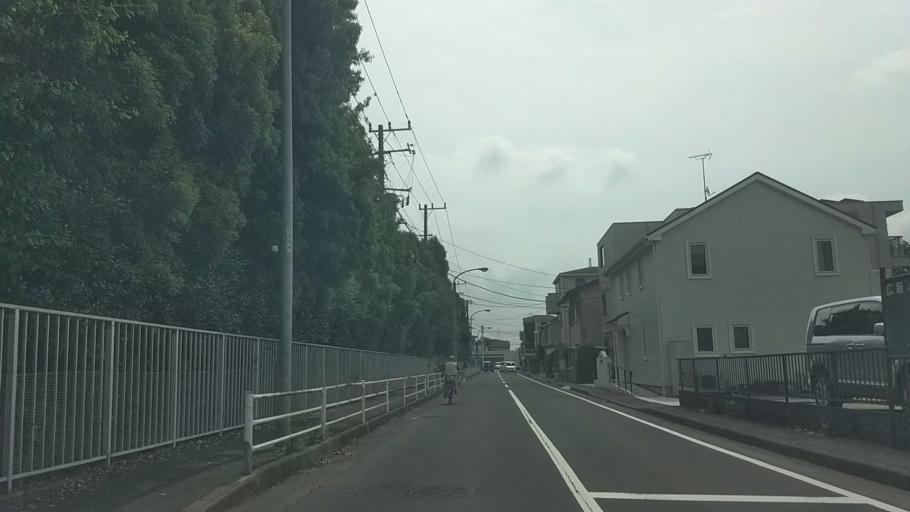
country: JP
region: Kanagawa
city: Fujisawa
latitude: 35.3592
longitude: 139.4768
